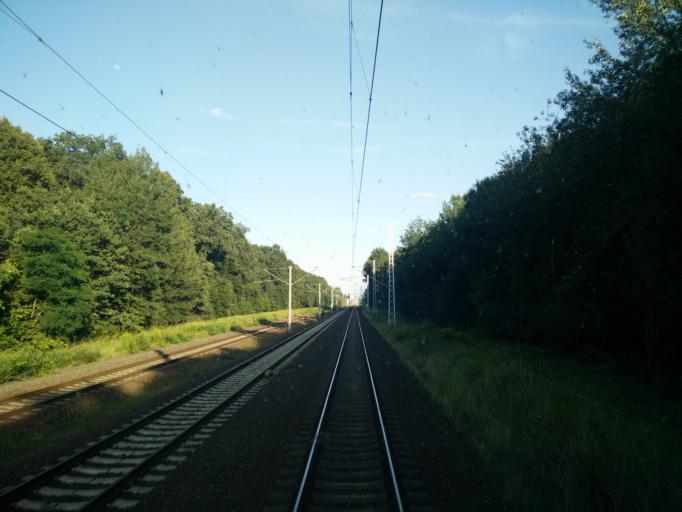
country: DE
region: Brandenburg
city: Paulinenaue
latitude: 52.6718
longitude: 12.7226
